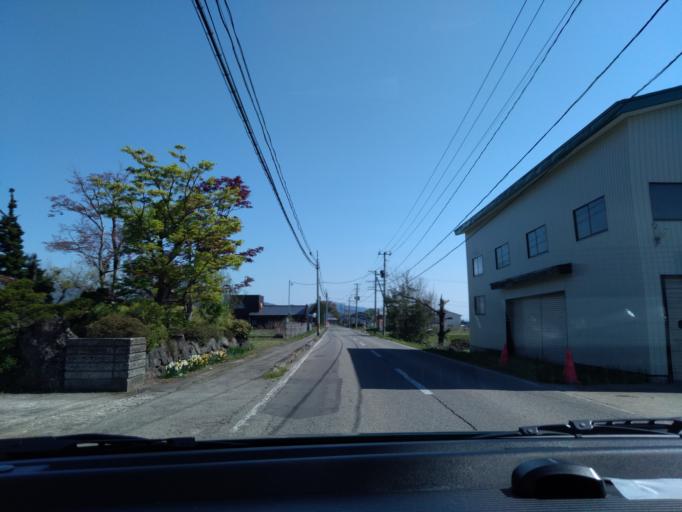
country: JP
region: Akita
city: Kakunodatemachi
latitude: 39.5208
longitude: 140.5885
